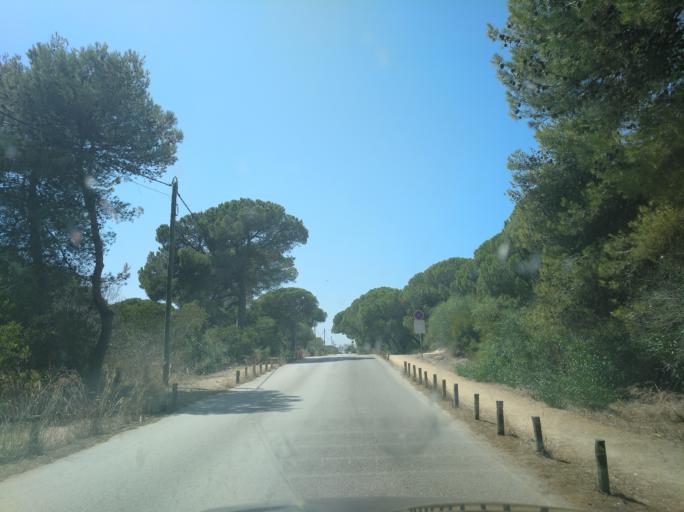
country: PT
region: Setubal
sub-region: Almada
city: Trafaria
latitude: 38.6601
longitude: -9.2472
